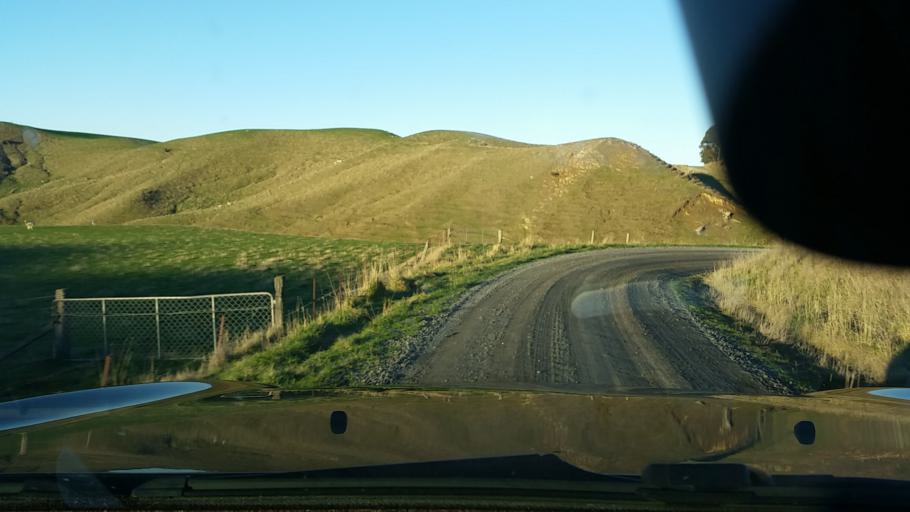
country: NZ
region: Marlborough
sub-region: Marlborough District
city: Blenheim
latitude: -41.7489
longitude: 174.0668
